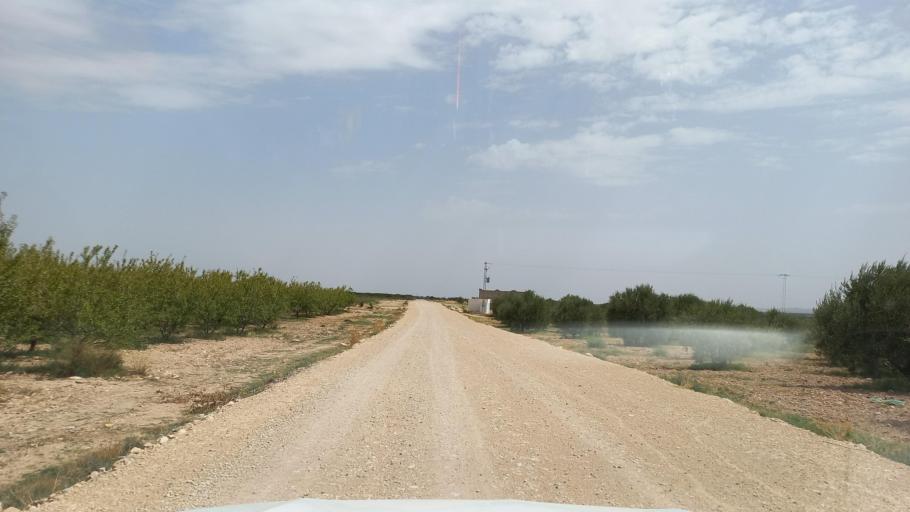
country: TN
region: Al Qasrayn
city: Kasserine
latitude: 35.2815
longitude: 9.0083
